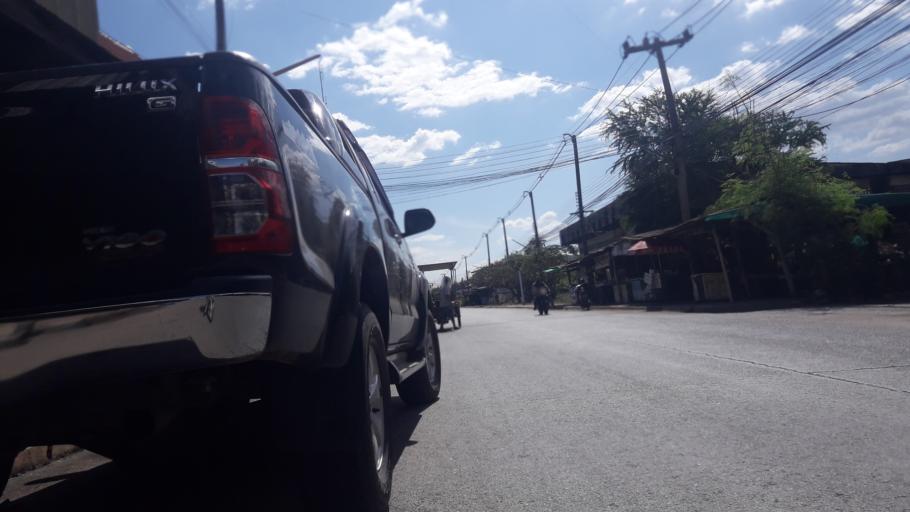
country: TH
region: Phichit
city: Thap Khlo
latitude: 16.1684
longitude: 100.5758
